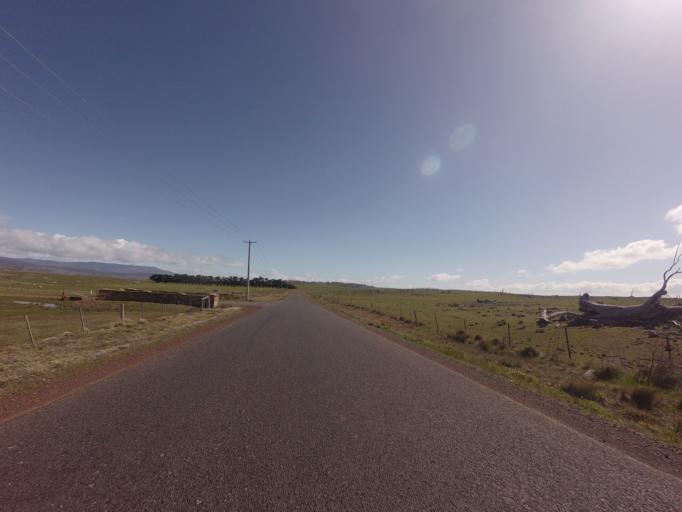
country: AU
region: Tasmania
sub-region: Northern Midlands
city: Evandale
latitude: -41.9002
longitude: 147.4408
